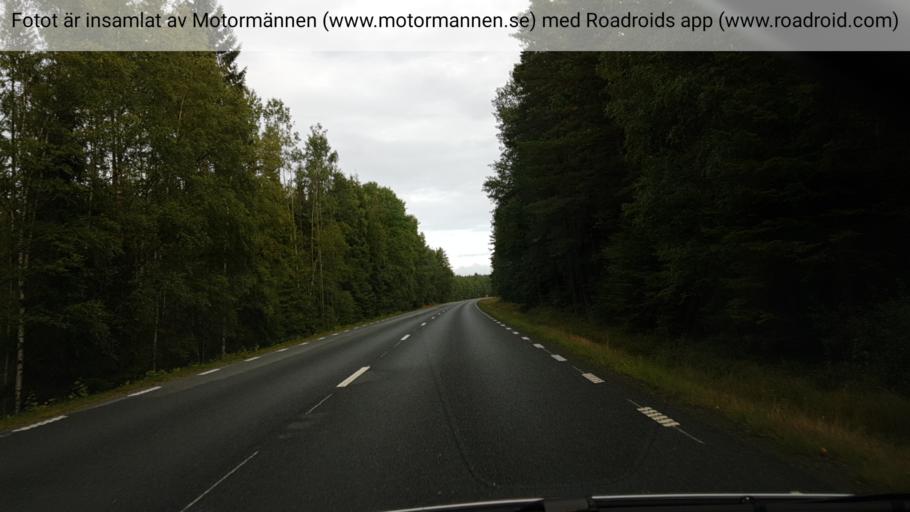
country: SE
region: Vaestra Goetaland
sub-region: Tidaholms Kommun
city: Olofstorp
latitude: 58.2143
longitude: 14.0800
